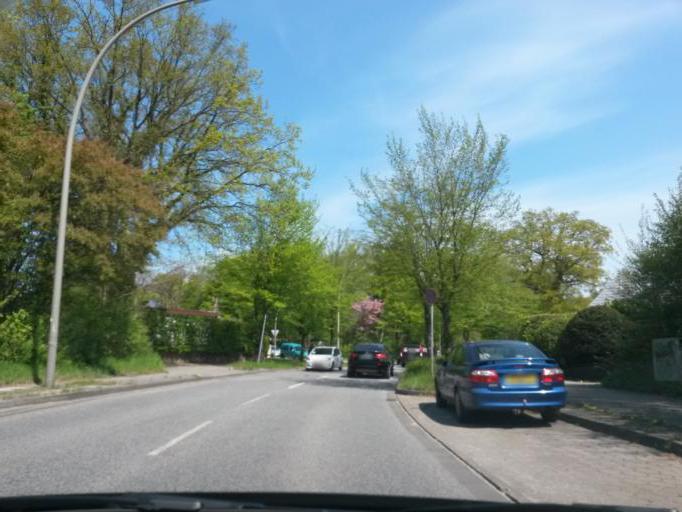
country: DE
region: Hamburg
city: Eidelstedt
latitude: 53.5626
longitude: 9.8640
